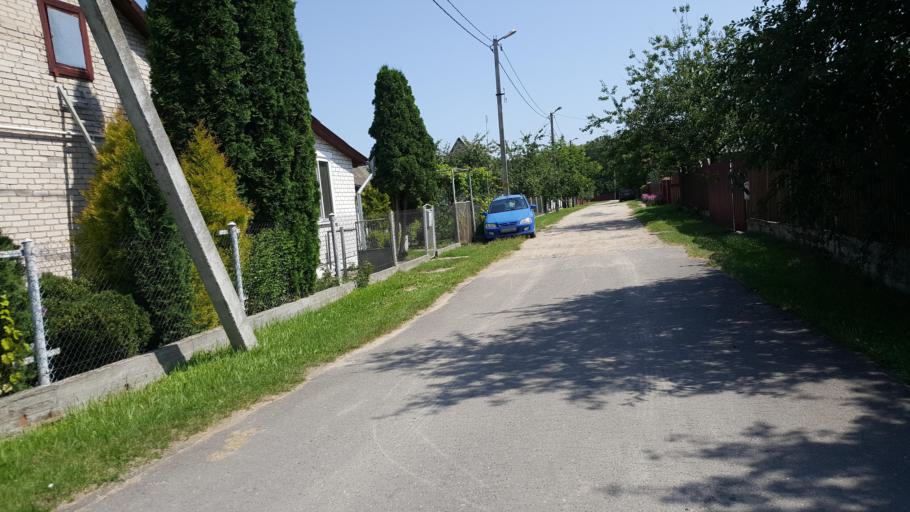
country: BY
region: Brest
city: Zhabinka
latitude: 52.1918
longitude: 24.0108
